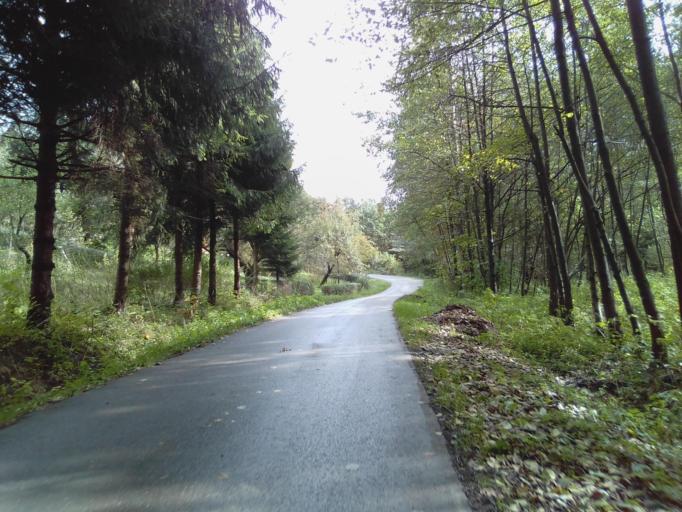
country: PL
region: Subcarpathian Voivodeship
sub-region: Powiat strzyzowski
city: Gwoznica Gorna
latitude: 49.8336
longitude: 22.0023
